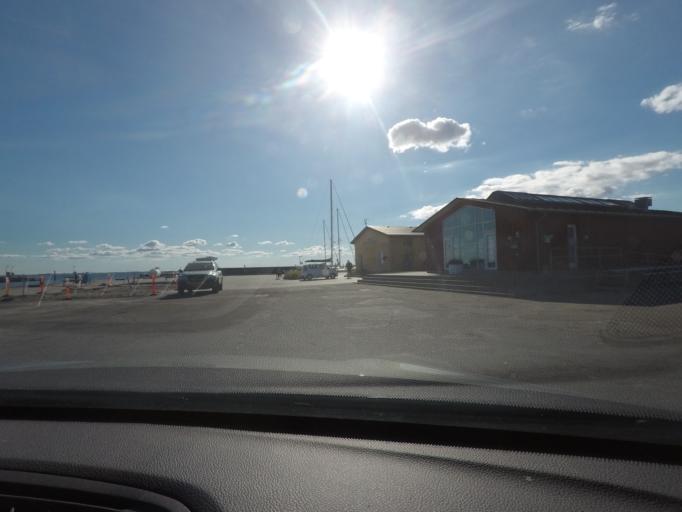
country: DK
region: Zealand
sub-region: Lolland Kommune
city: Maribo
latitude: 54.9730
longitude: 11.5140
